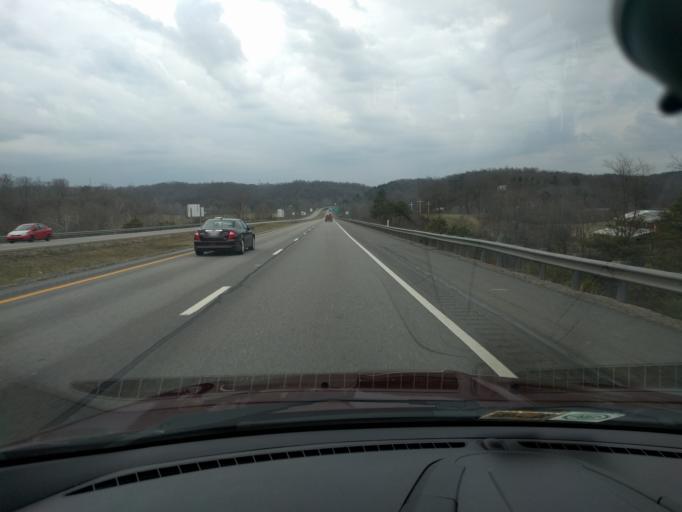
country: US
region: West Virginia
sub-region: Wood County
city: Parkersburg
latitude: 39.2787
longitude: -81.4942
